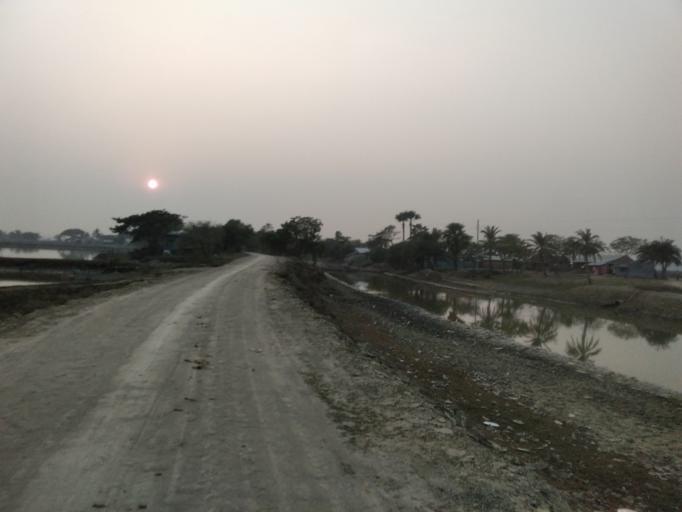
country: BD
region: Khulna
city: Satkhira
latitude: 22.6517
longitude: 89.0175
